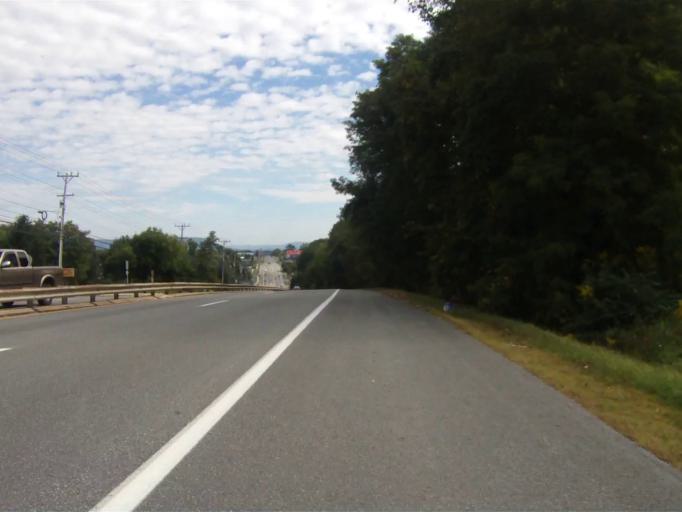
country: US
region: Pennsylvania
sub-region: Centre County
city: Park Forest Village
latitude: 40.8109
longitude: -77.9194
